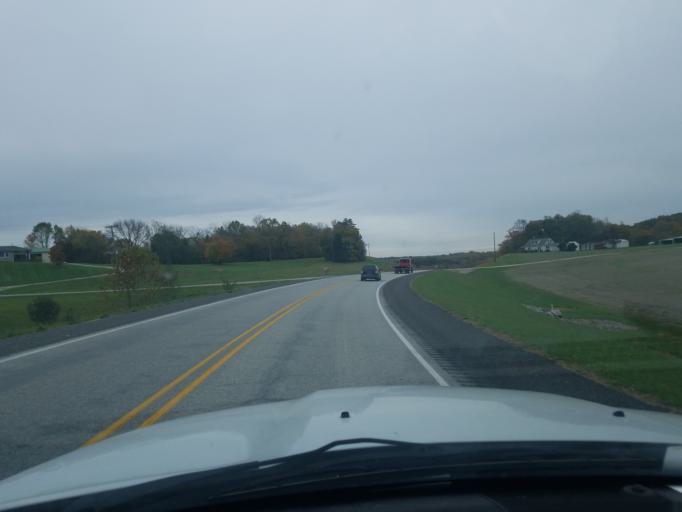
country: US
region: Indiana
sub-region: Washington County
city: Salem
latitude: 38.5352
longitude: -86.1002
